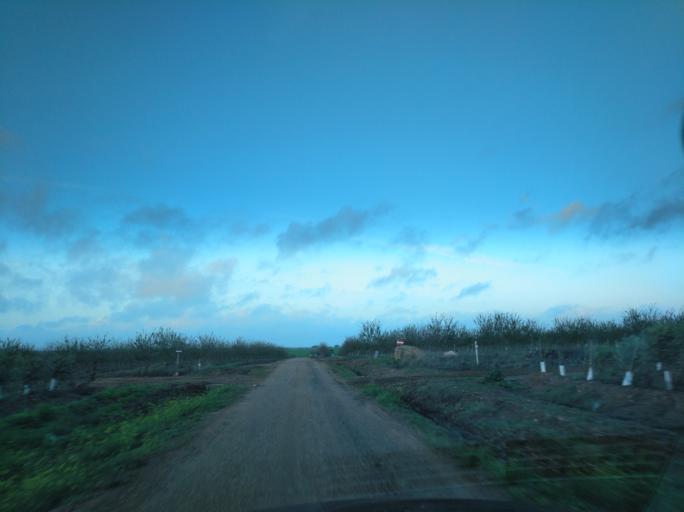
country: PT
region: Portalegre
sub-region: Campo Maior
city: Campo Maior
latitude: 39.0267
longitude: -7.1268
